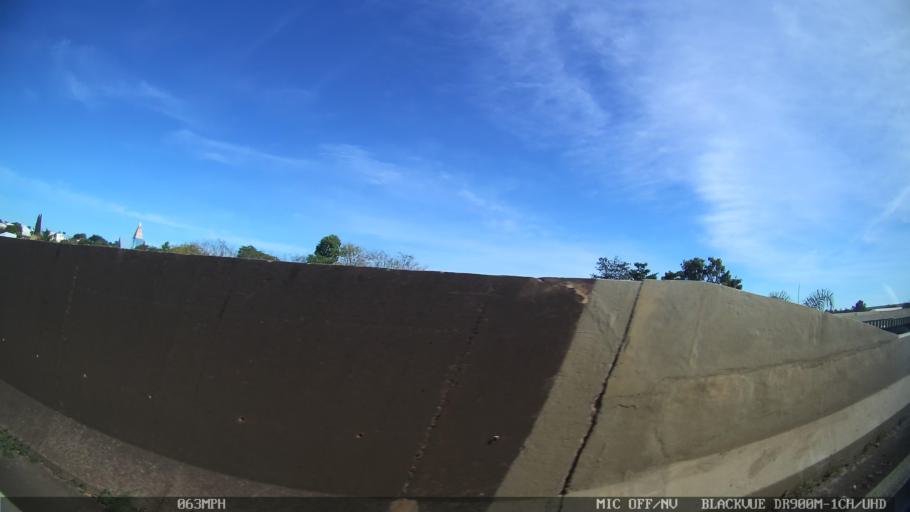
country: BR
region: Sao Paulo
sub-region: Araras
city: Araras
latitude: -22.3493
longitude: -47.3944
